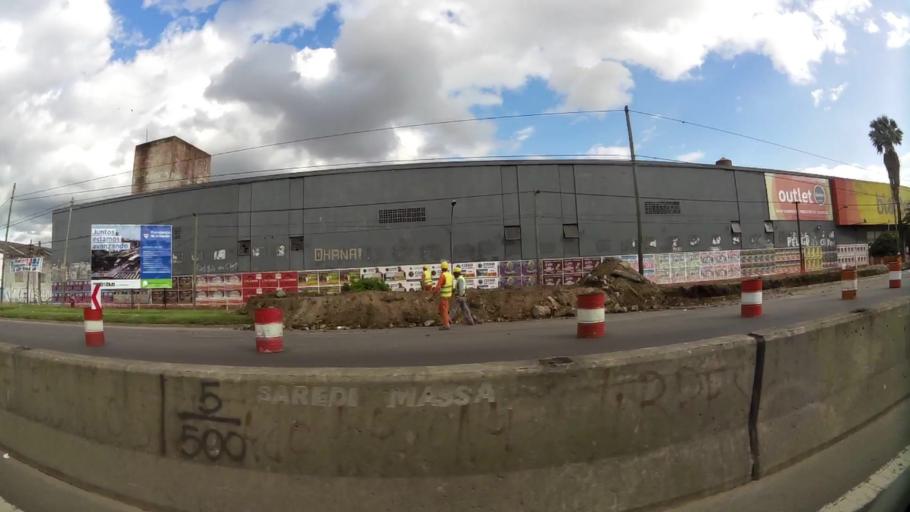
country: AR
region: Buenos Aires
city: San Justo
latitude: -34.6896
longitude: -58.5677
